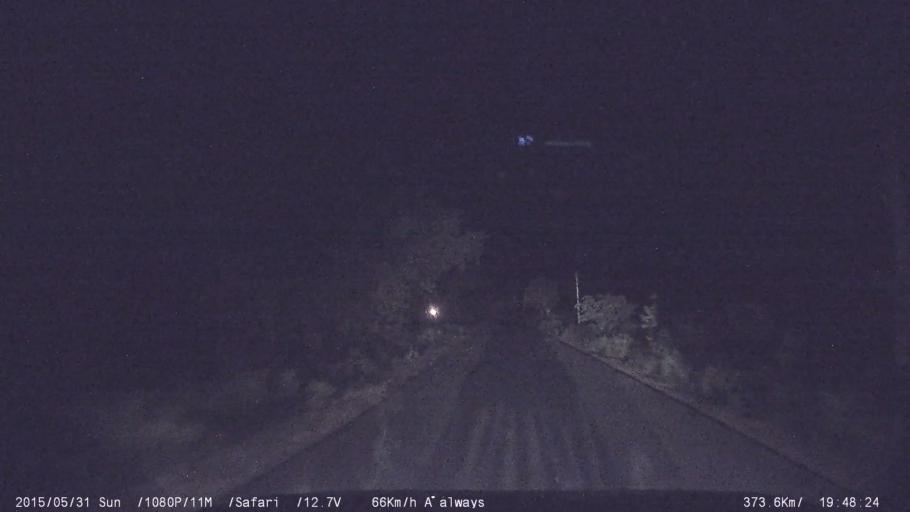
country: IN
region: Karnataka
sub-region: Mandya
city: Malavalli
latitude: 12.3087
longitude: 77.0725
